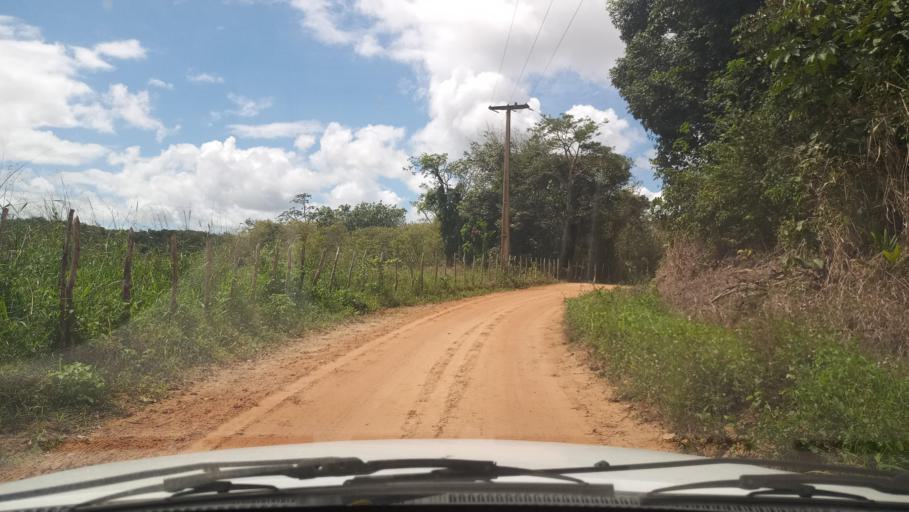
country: BR
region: Rio Grande do Norte
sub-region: Goianinha
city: Goianinha
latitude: -6.2603
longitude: -35.2477
